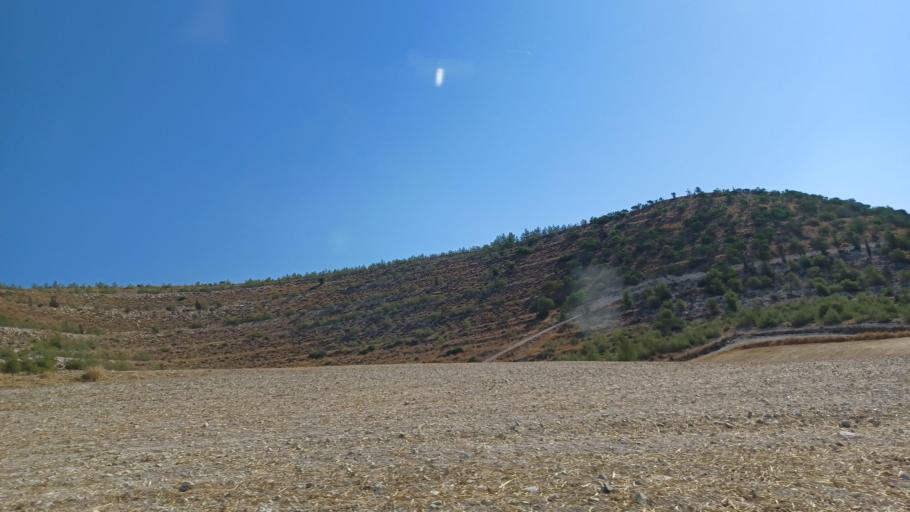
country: CY
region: Lefkosia
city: Lympia
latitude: 34.9780
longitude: 33.4961
